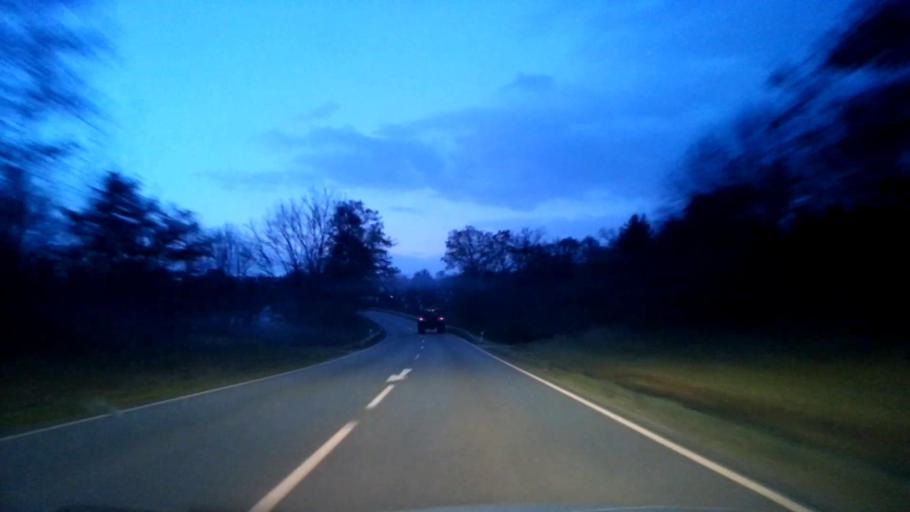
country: DE
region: Bavaria
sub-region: Upper Franconia
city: Reuth
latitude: 49.9565
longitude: 11.7045
